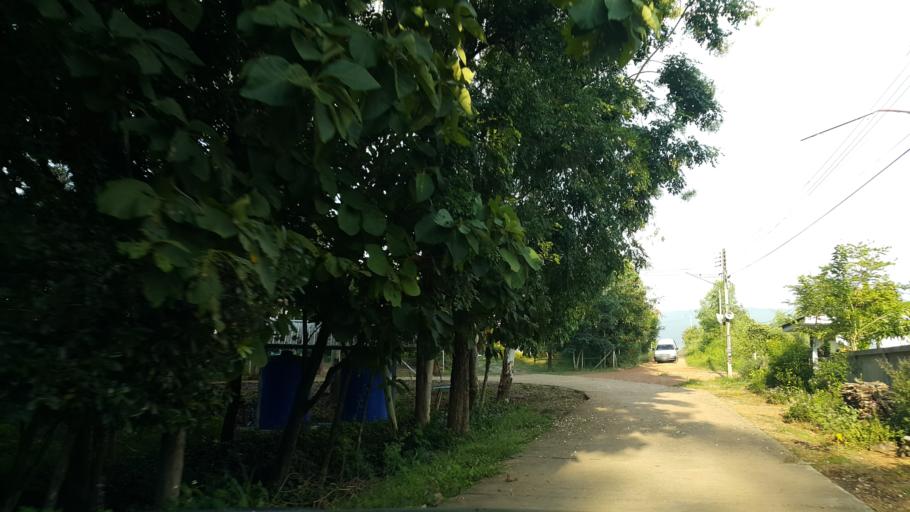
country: TH
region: Chiang Mai
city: Mae On
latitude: 18.7388
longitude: 99.2383
